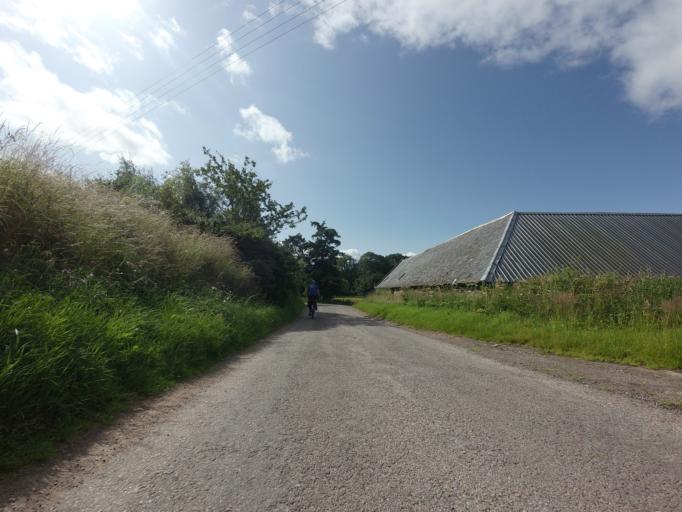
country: GB
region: Scotland
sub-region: Highland
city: Nairn
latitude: 57.5544
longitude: -3.8662
